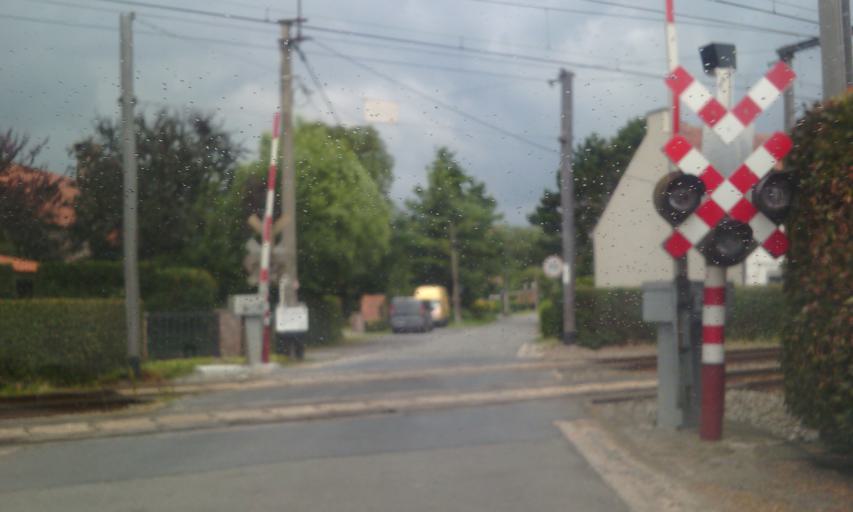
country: BE
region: Flanders
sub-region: Provincie Oost-Vlaanderen
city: Lokeren
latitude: 51.0988
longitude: 3.9474
